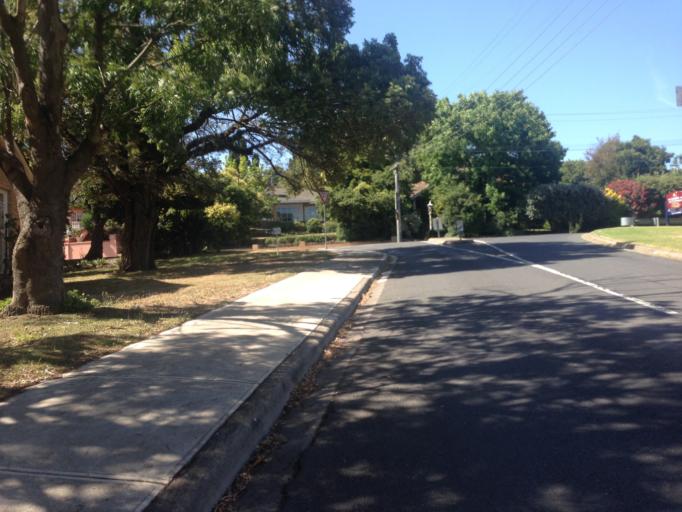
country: AU
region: Victoria
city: Ivanhoe East
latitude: -37.7787
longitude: 145.0572
